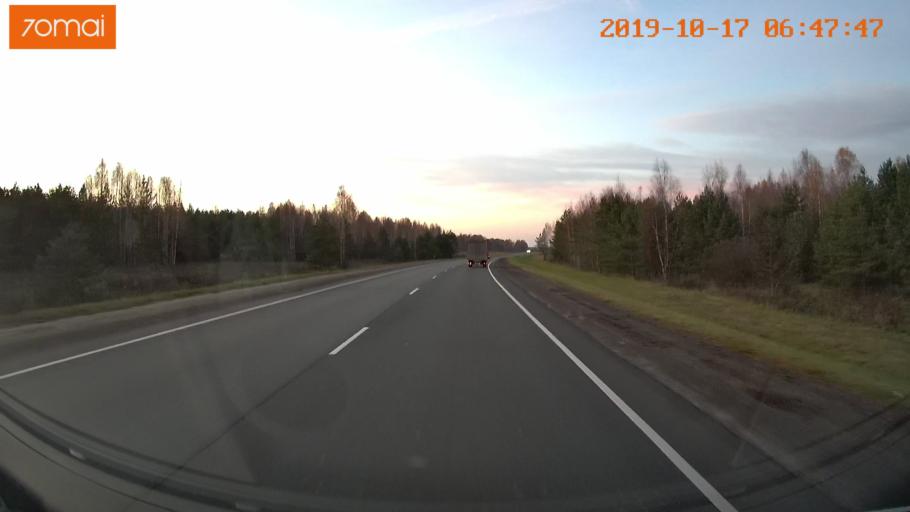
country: RU
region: Vladimir
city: Kideksha
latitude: 56.5316
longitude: 40.5582
